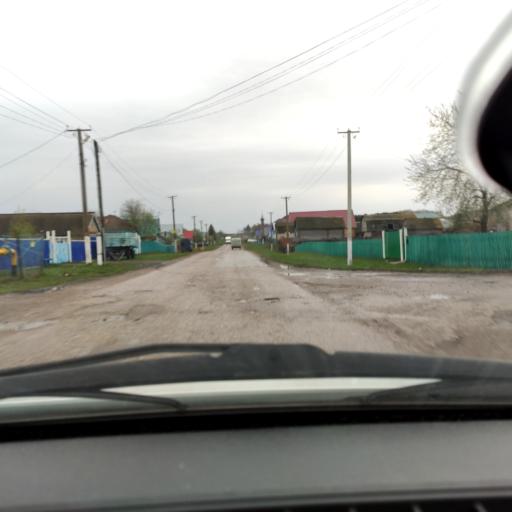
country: RU
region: Bashkortostan
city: Tolbazy
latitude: 54.1722
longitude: 55.9536
